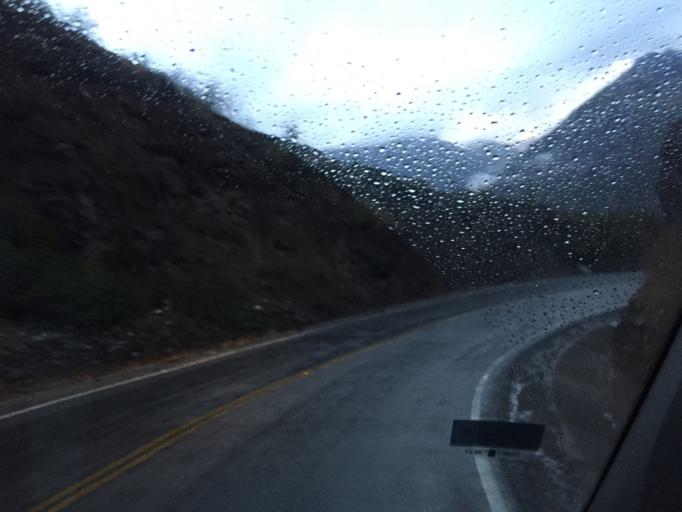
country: PE
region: Cusco
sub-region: Provincia de Urubamba
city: Urubamba
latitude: -13.3114
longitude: -72.1205
